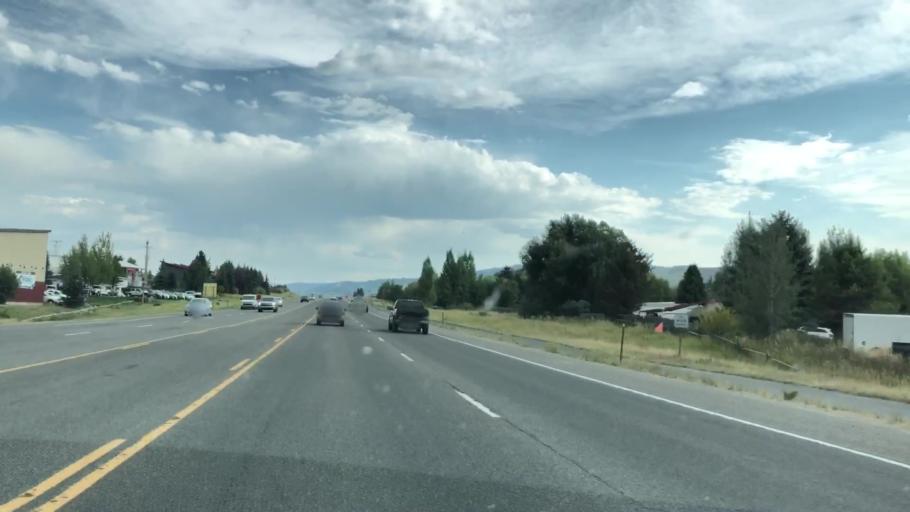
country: US
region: Wyoming
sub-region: Teton County
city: South Park
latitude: 43.4253
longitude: -110.7779
